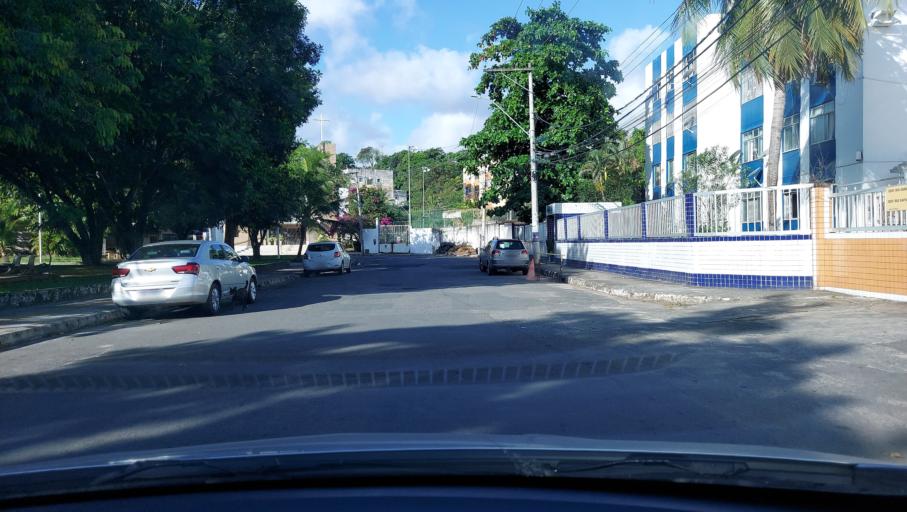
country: BR
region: Bahia
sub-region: Salvador
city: Salvador
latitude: -12.9793
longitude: -38.4476
